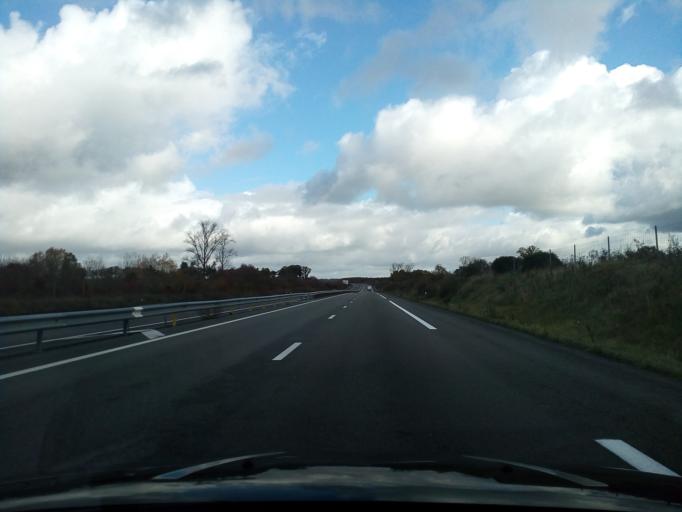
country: FR
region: Limousin
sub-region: Departement de la Creuse
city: Gouzon
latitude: 46.2026
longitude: 2.2622
